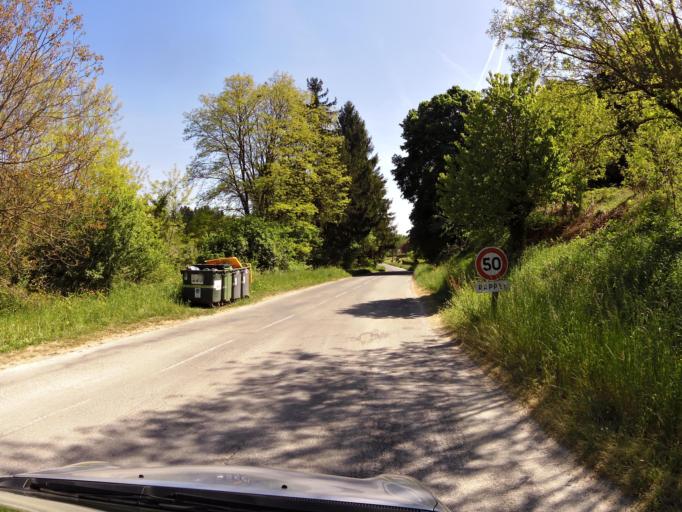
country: FR
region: Aquitaine
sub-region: Departement de la Dordogne
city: Sarlat-la-Caneda
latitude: 44.9132
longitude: 1.2047
